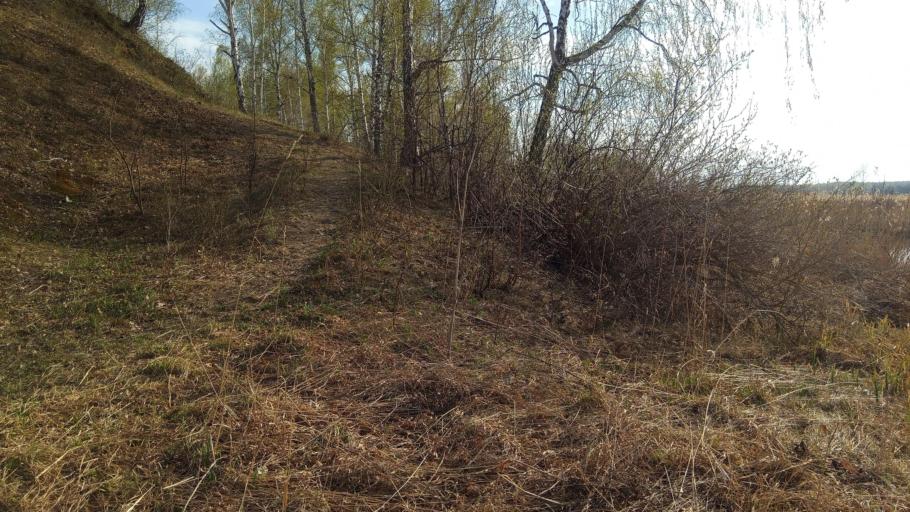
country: RU
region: Chelyabinsk
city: Poletayevo
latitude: 55.0315
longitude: 61.0740
